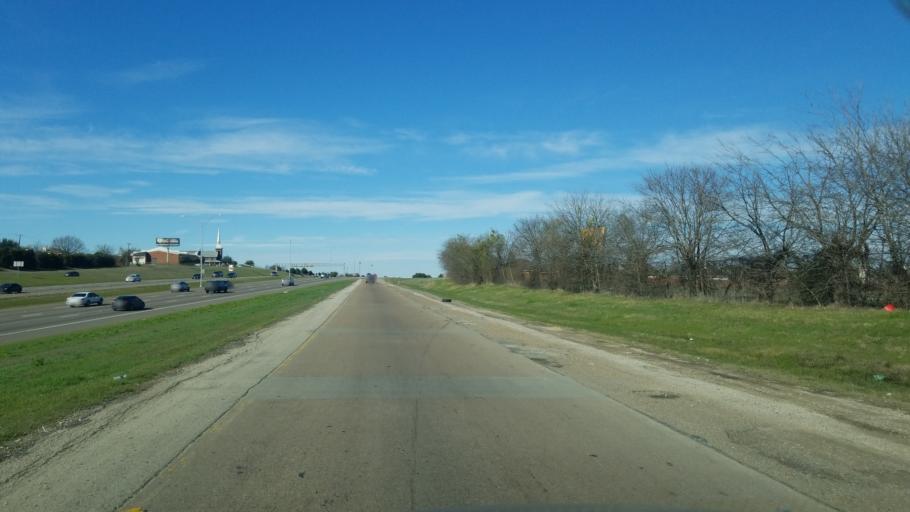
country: US
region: Texas
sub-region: Dallas County
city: Balch Springs
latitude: 32.7493
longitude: -96.6136
